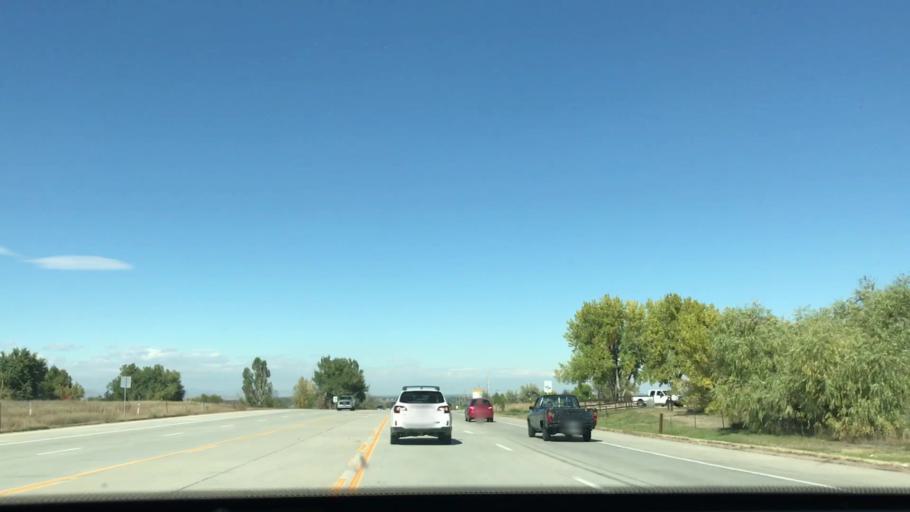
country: US
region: Colorado
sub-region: Boulder County
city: Lafayette
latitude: 40.0183
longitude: -105.1029
